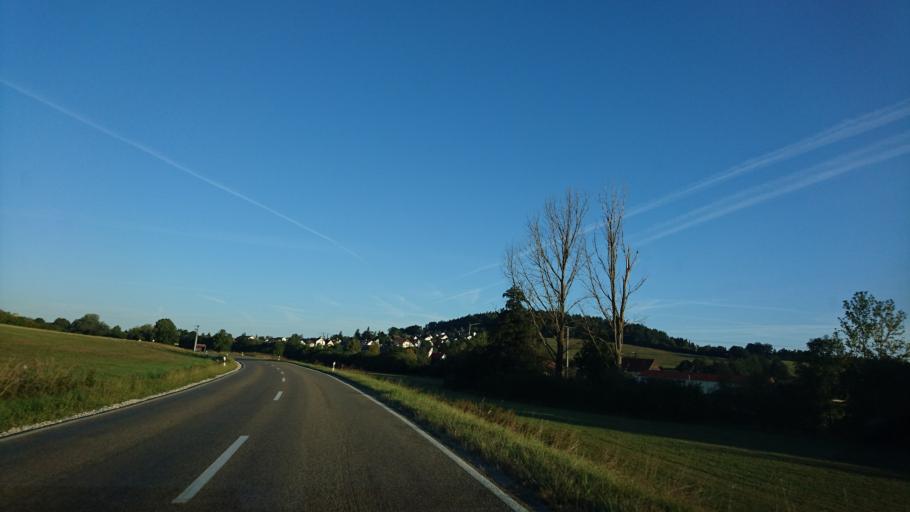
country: DE
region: Bavaria
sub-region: Regierungsbezirk Mittelfranken
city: Thalmassing
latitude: 49.0861
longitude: 11.2380
